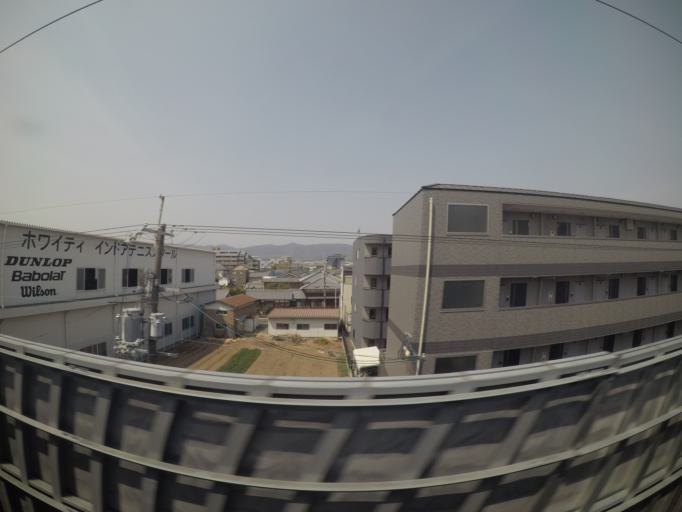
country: JP
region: Kyoto
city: Muko
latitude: 34.9622
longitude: 135.7153
